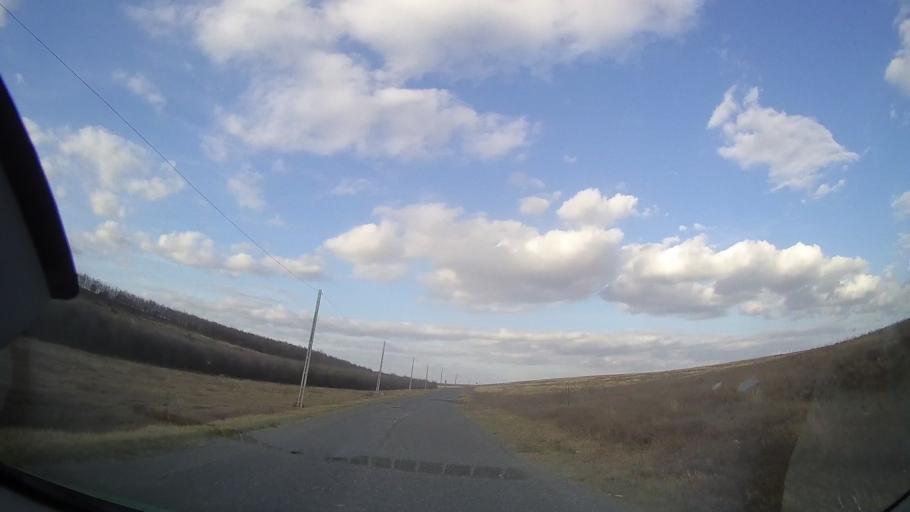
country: RO
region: Constanta
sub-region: Comuna Cerchezu
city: Cerchezu
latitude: 43.8316
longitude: 28.0961
